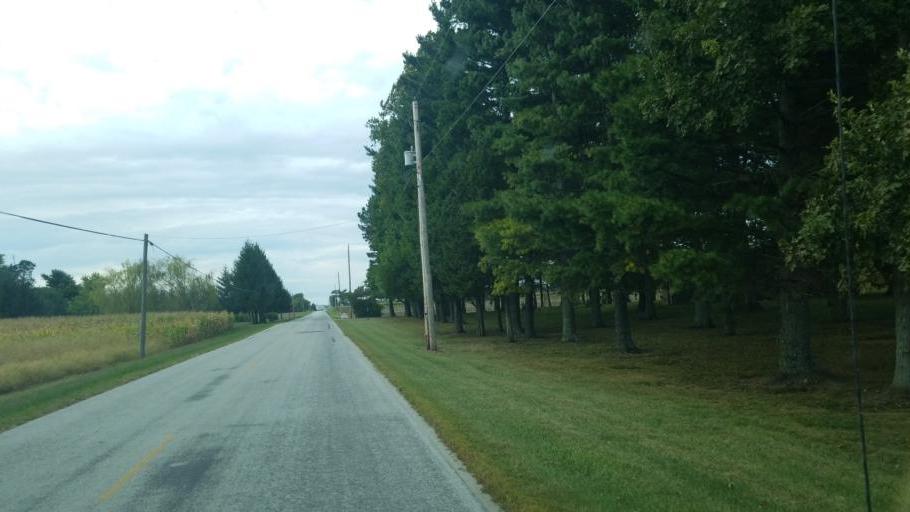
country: US
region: Ohio
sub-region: Hardin County
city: Forest
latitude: 40.6868
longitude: -83.4800
